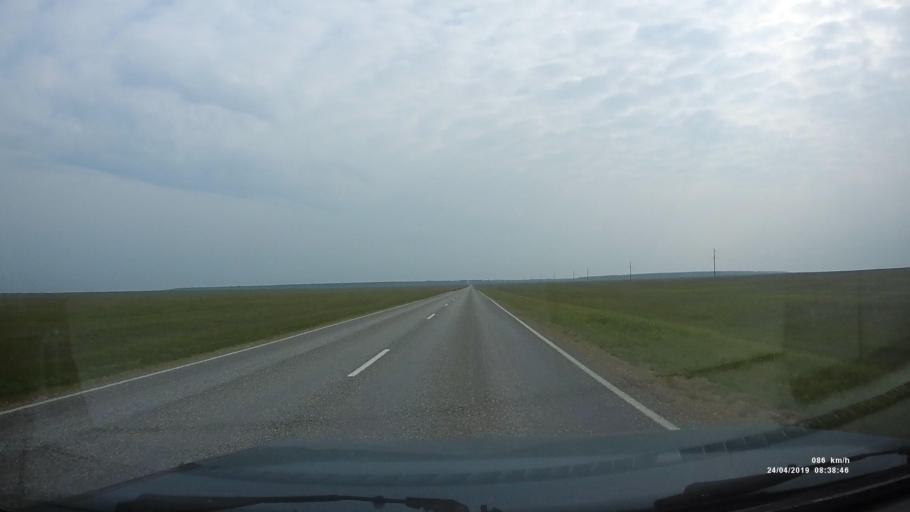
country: RU
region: Kalmykiya
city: Arshan'
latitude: 46.2173
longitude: 43.9729
